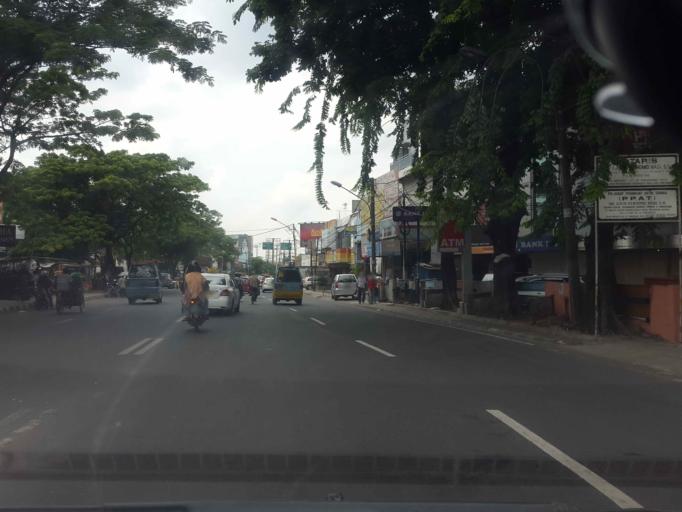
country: ID
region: Banten
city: Tangerang
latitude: -6.1757
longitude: 106.6275
